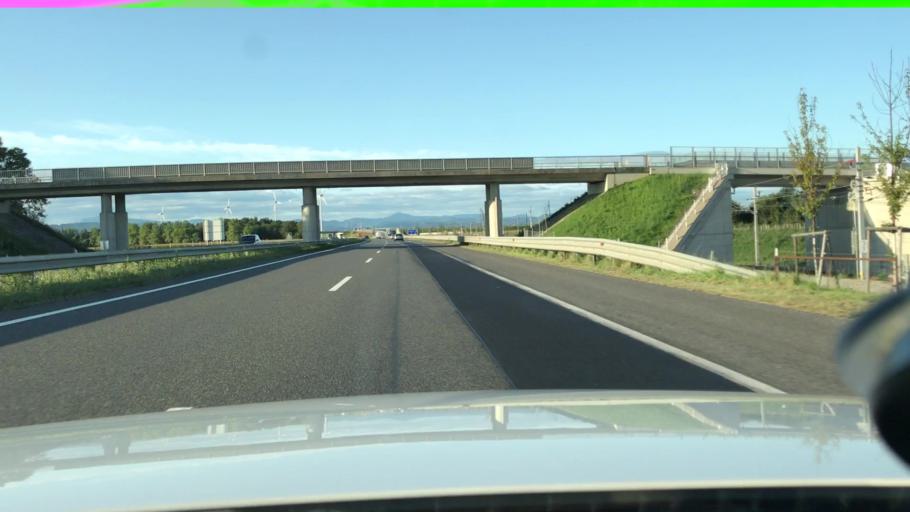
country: AT
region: Lower Austria
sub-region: Sankt Polten Stadt
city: Sankt Poelten
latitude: 48.2060
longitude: 15.6655
